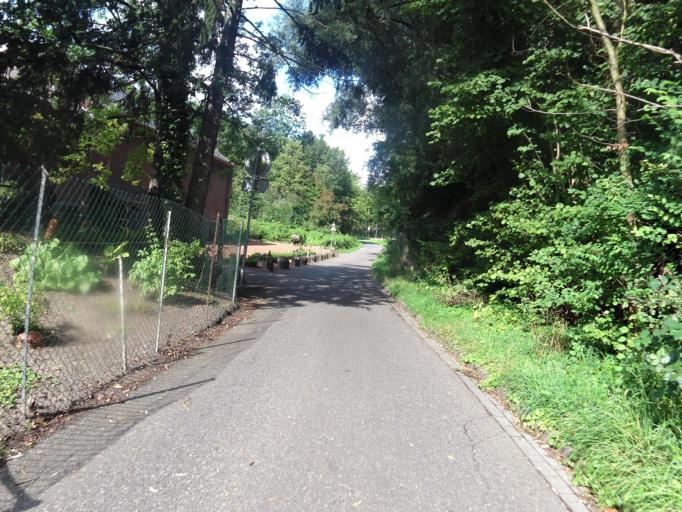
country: NL
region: Limburg
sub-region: Gemeente Heerlen
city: Nieuw-Lotbroek
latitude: 50.9084
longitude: 5.9506
